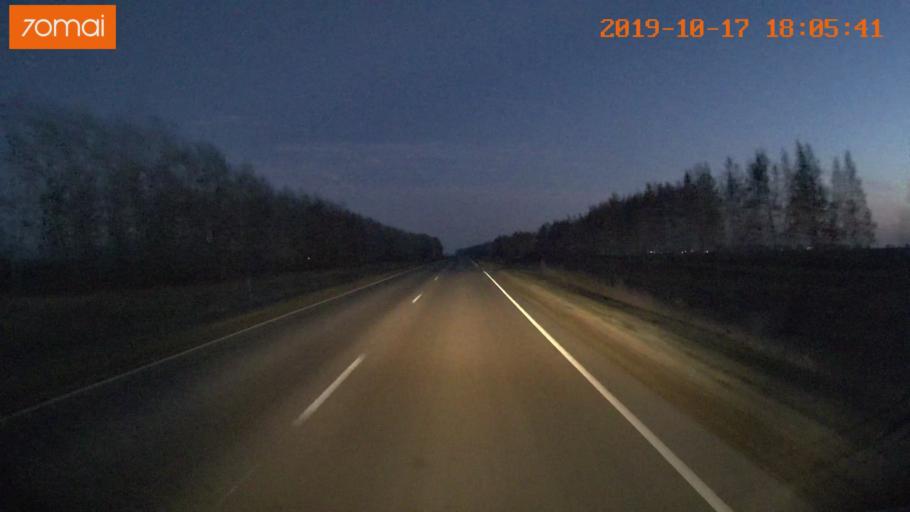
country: RU
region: Tula
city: Kurkino
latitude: 53.4627
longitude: 38.6468
